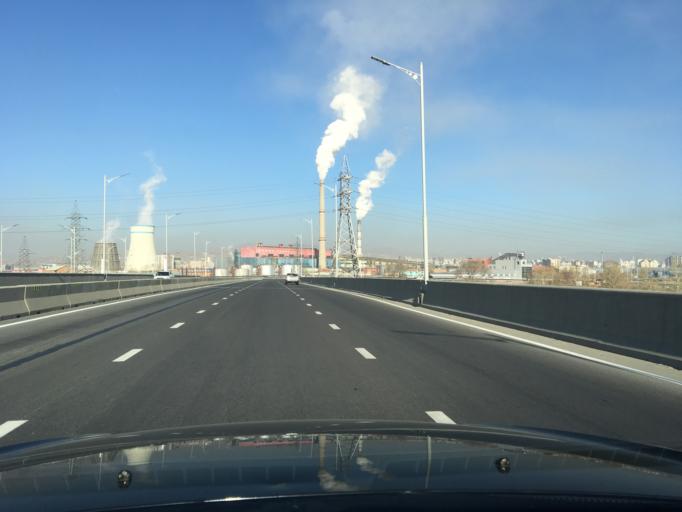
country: MN
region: Ulaanbaatar
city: Ulaanbaatar
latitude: 47.8873
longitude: 106.8642
